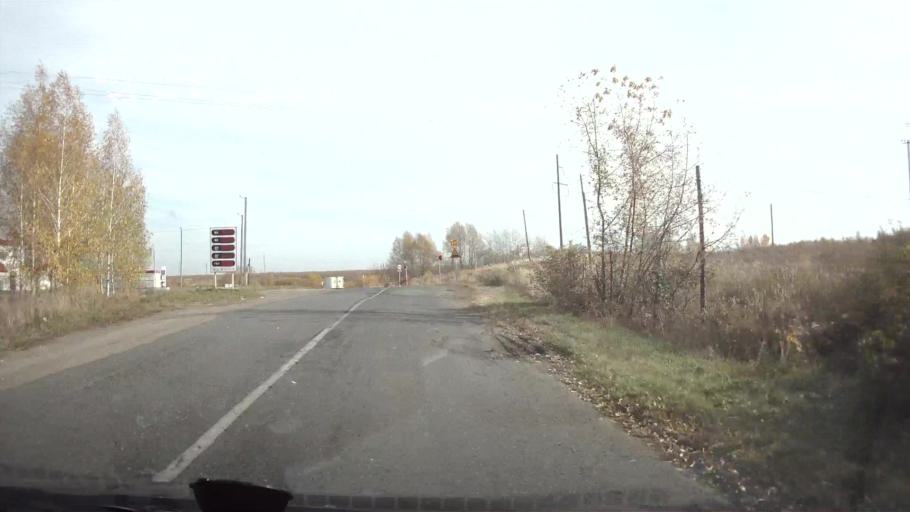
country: RU
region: Chuvashia
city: Alatyr'
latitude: 54.8433
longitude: 46.4738
